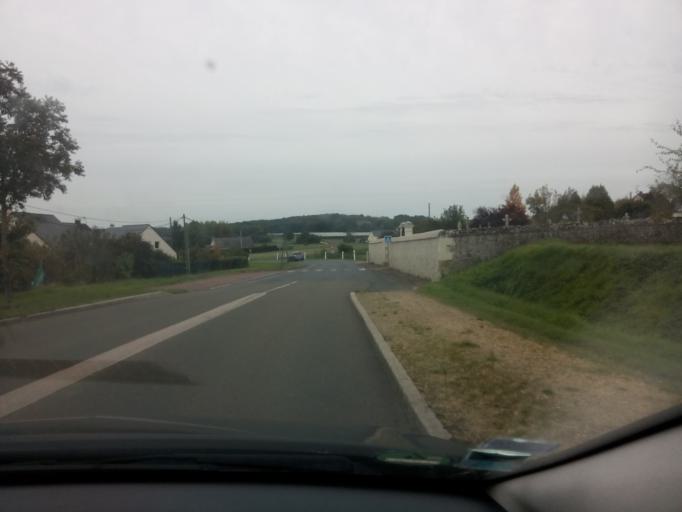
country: FR
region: Pays de la Loire
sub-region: Departement de Maine-et-Loire
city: Baune
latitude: 47.5017
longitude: -0.3227
